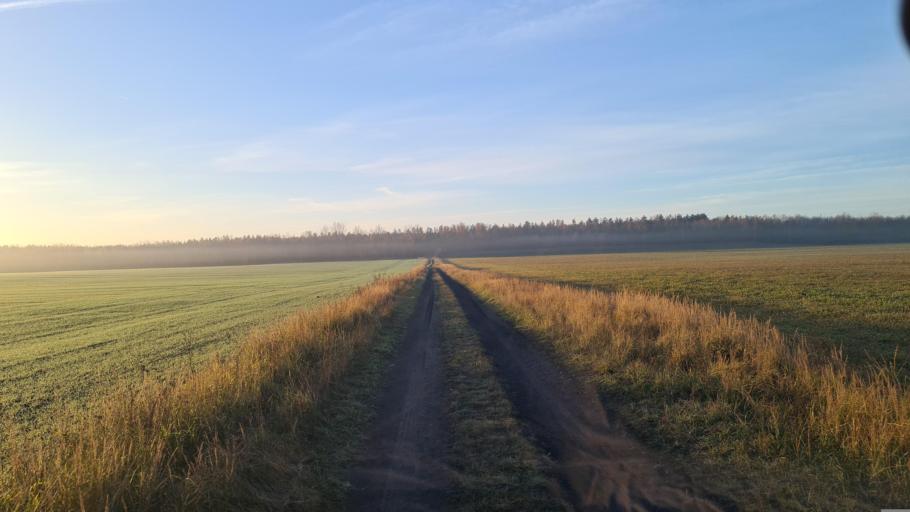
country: DE
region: Brandenburg
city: Lauchhammer
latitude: 51.5443
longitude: 13.7568
